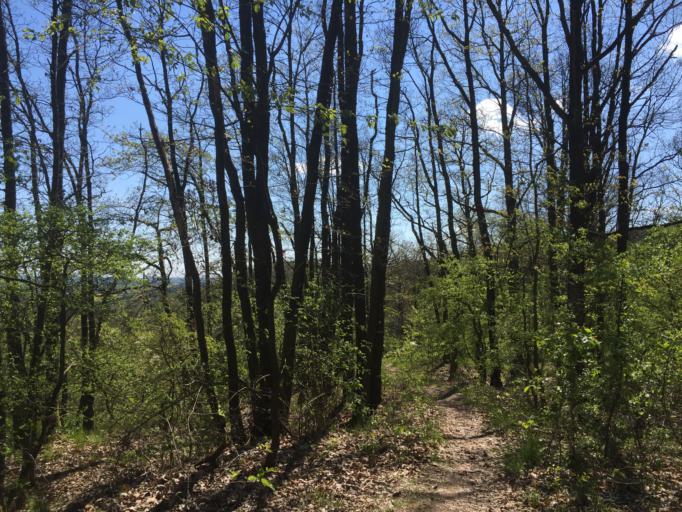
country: DE
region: Bavaria
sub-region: Regierungsbezirk Unterfranken
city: Sulzfeld
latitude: 50.2738
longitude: 10.4187
